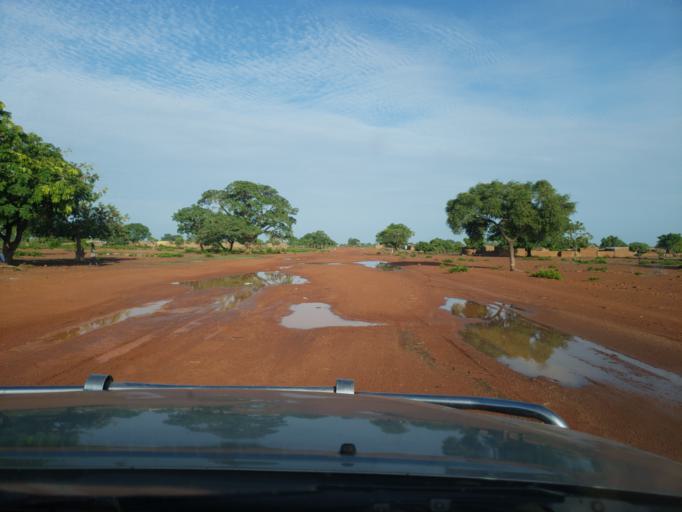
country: ML
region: Sikasso
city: Koutiala
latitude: 12.4289
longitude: -5.6189
